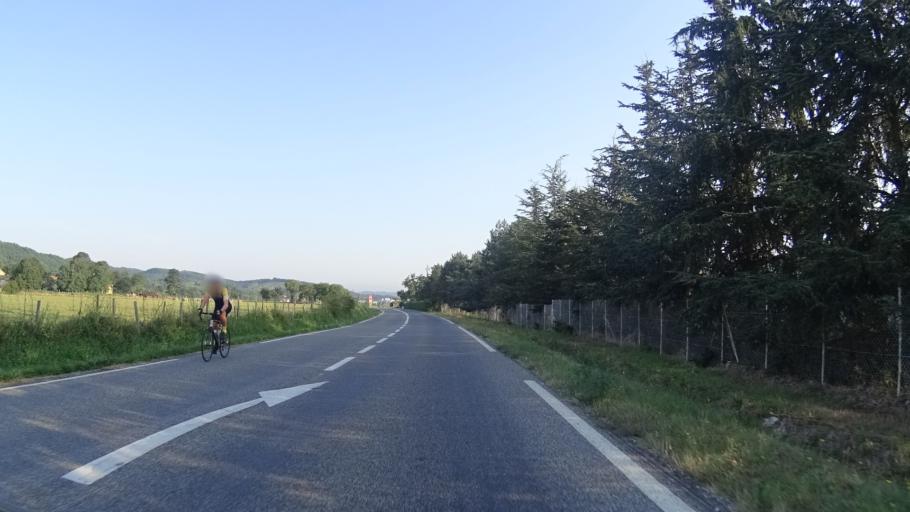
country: FR
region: Midi-Pyrenees
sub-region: Departement de l'Ariege
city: Mirepoix
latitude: 43.0448
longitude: 1.8950
